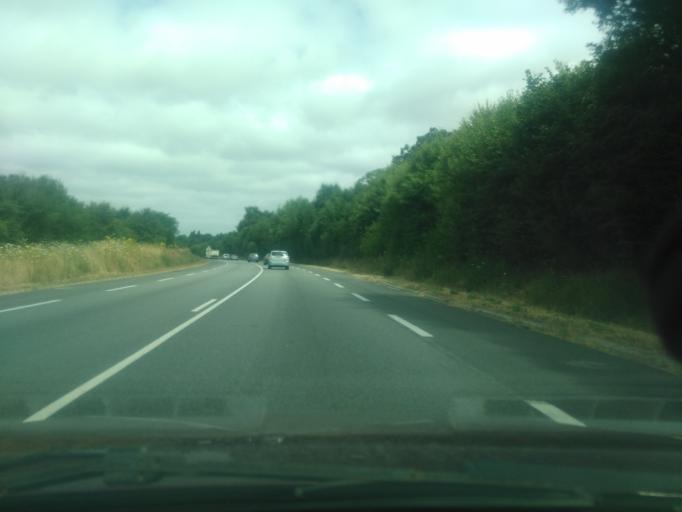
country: FR
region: Pays de la Loire
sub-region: Departement de la Vendee
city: La Roche-sur-Yon
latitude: 46.6877
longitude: -1.4125
